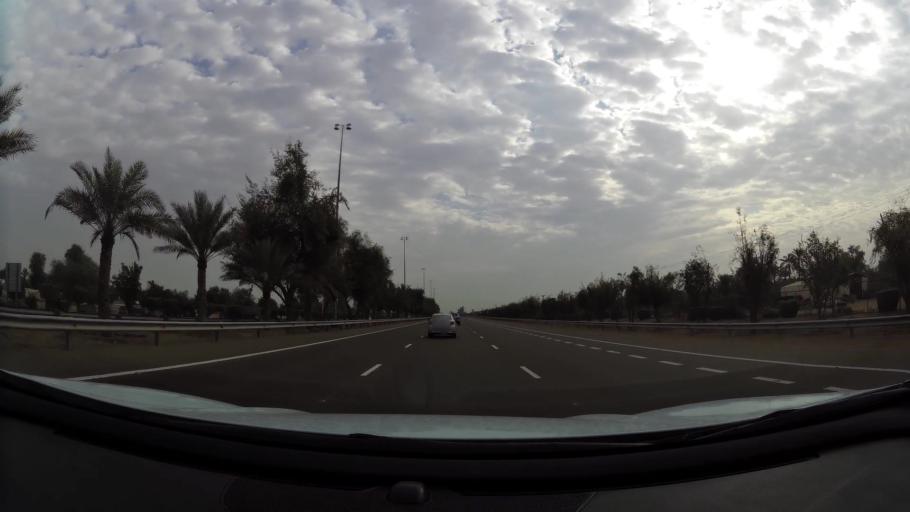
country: AE
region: Abu Dhabi
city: Al Ain
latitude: 24.1837
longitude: 55.3353
